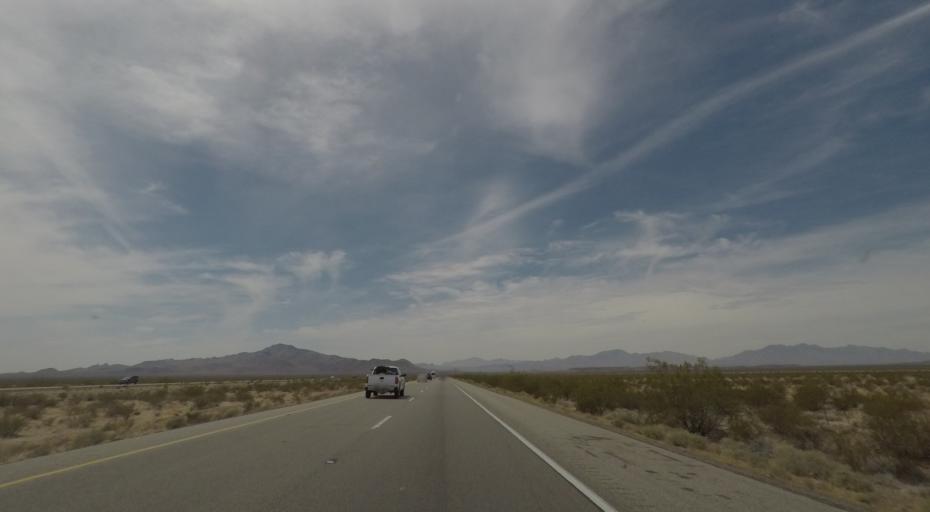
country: US
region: California
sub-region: San Bernardino County
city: Needles
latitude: 34.8085
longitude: -115.2328
